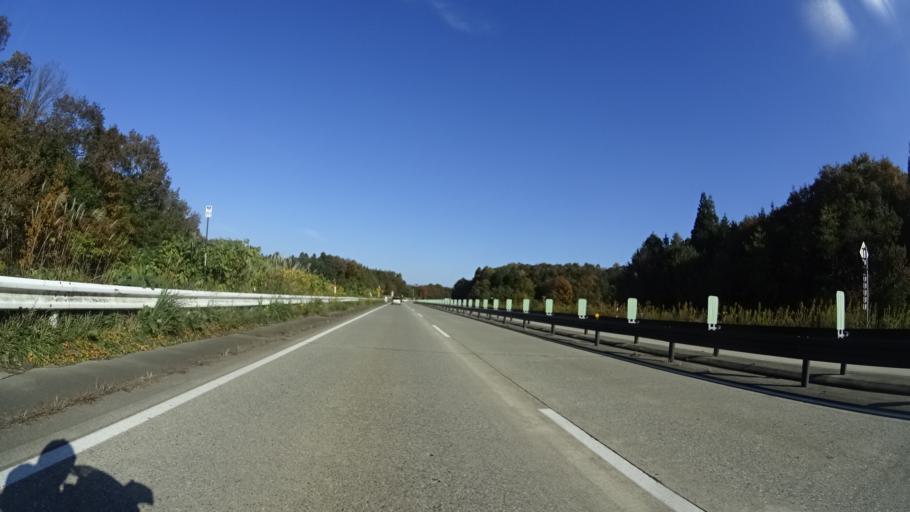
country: JP
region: Ishikawa
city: Komatsu
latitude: 36.3539
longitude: 136.4518
